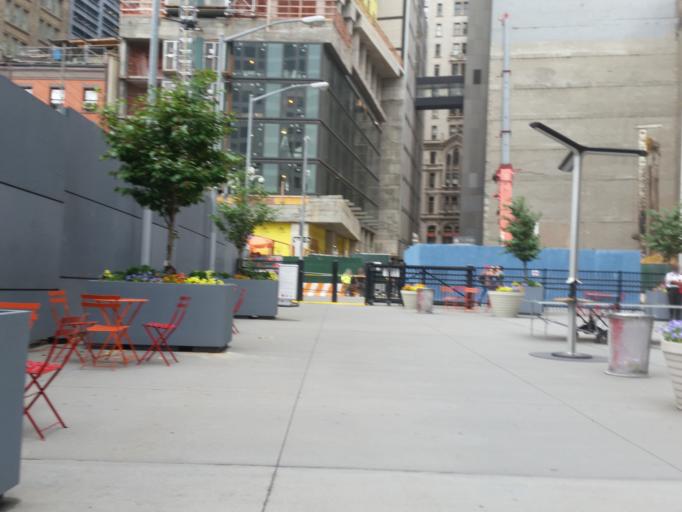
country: US
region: New York
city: New York City
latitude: 40.7106
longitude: -74.0134
